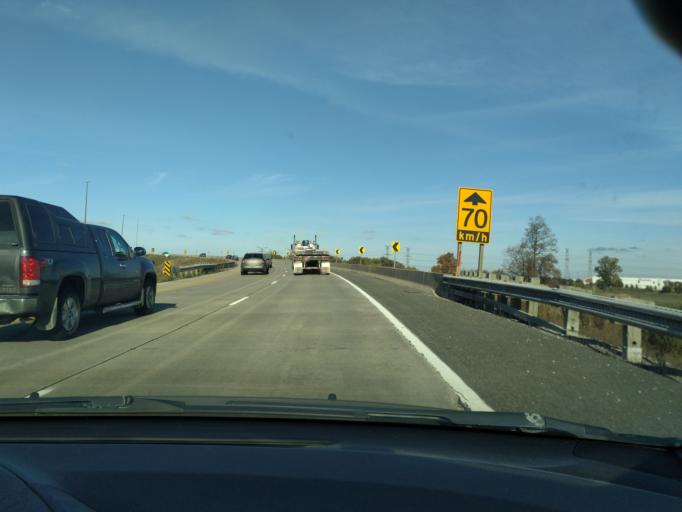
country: CA
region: Ontario
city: Brampton
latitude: 43.5940
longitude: -79.8016
